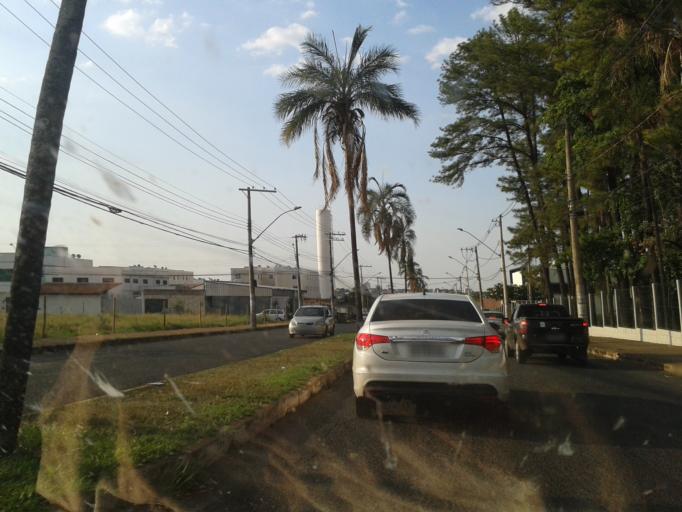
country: BR
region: Minas Gerais
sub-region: Uberlandia
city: Uberlandia
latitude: -18.9281
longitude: -48.3204
